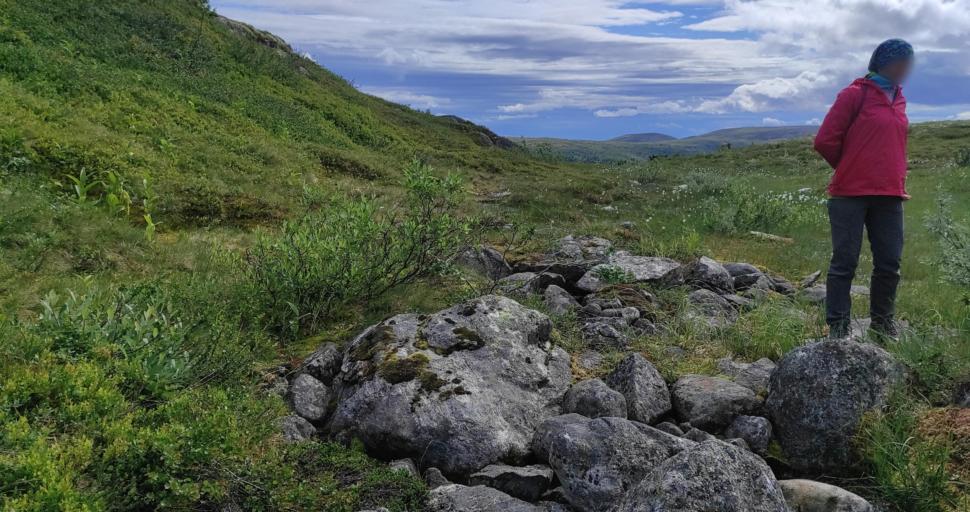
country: RU
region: Murmansk
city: Afrikanda
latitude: 67.0418
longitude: 32.9371
